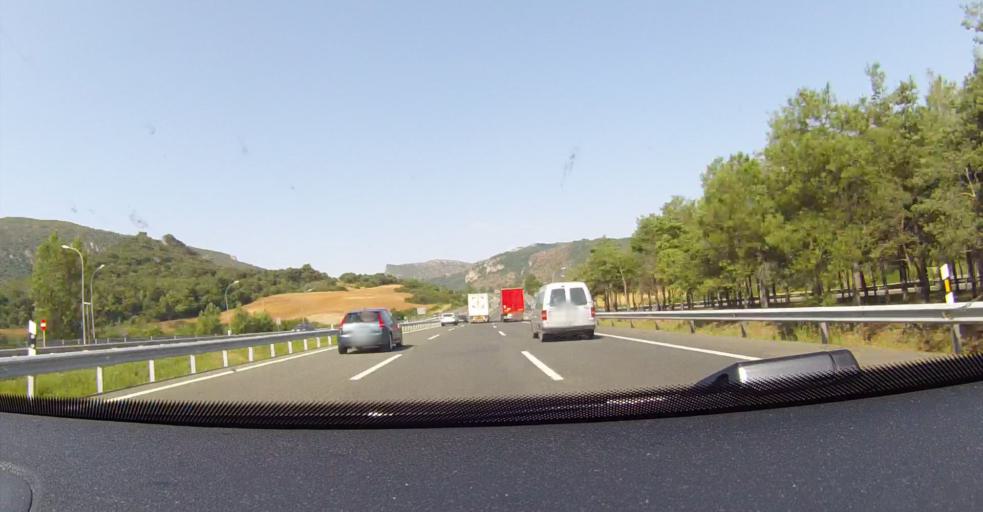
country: ES
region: Castille and Leon
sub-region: Provincia de Burgos
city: Ameyugo
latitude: 42.6514
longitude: -3.0703
